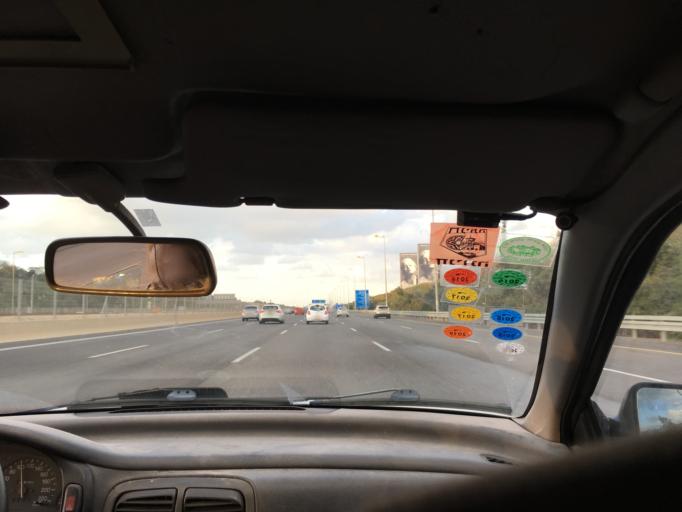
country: IL
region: Tel Aviv
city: Ramat HaSharon
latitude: 32.1227
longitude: 34.8107
